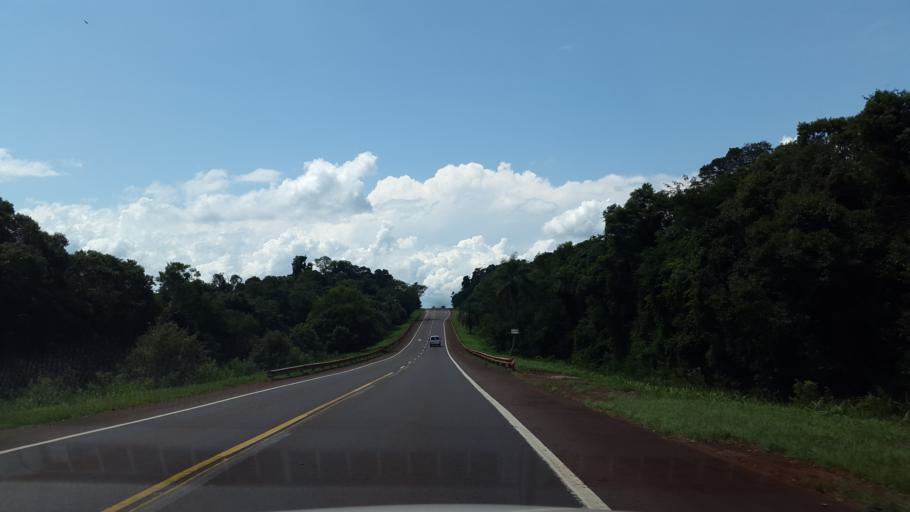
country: AR
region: Misiones
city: El Alcazar
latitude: -26.7014
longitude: -54.8391
